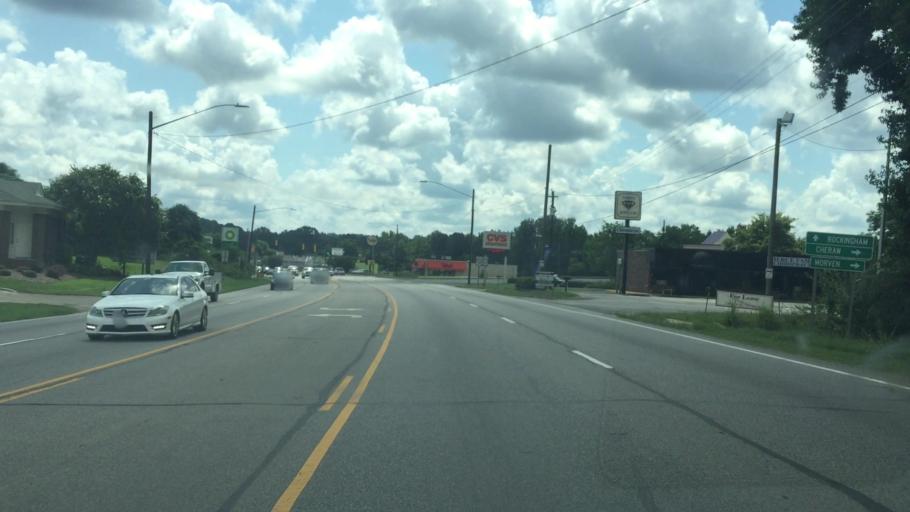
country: US
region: North Carolina
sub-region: Anson County
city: Wadesboro
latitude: 34.9643
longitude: -80.0587
